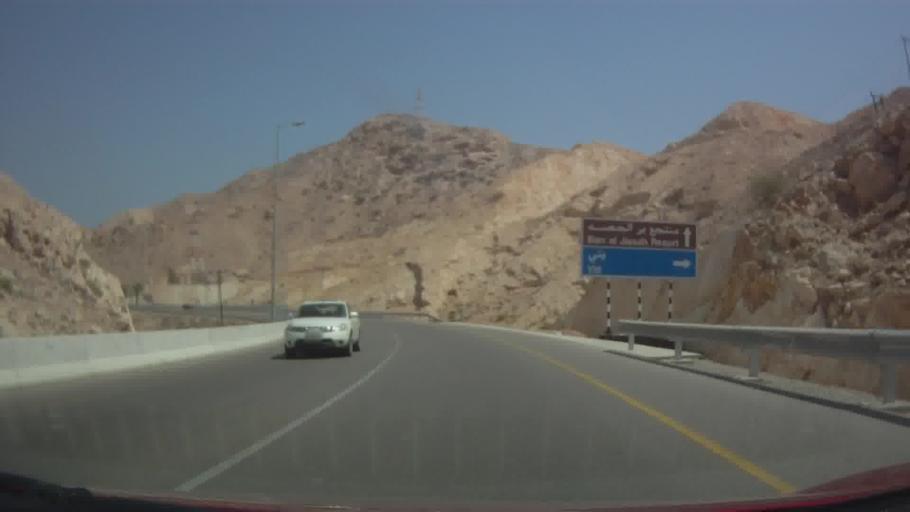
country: OM
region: Muhafazat Masqat
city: Muscat
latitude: 23.5410
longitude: 58.6448
